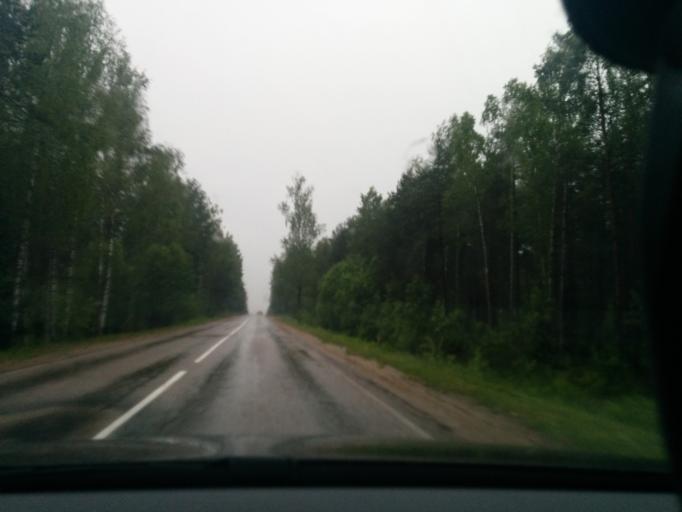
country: LV
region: Ogre
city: Ogre
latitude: 56.8465
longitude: 24.5722
